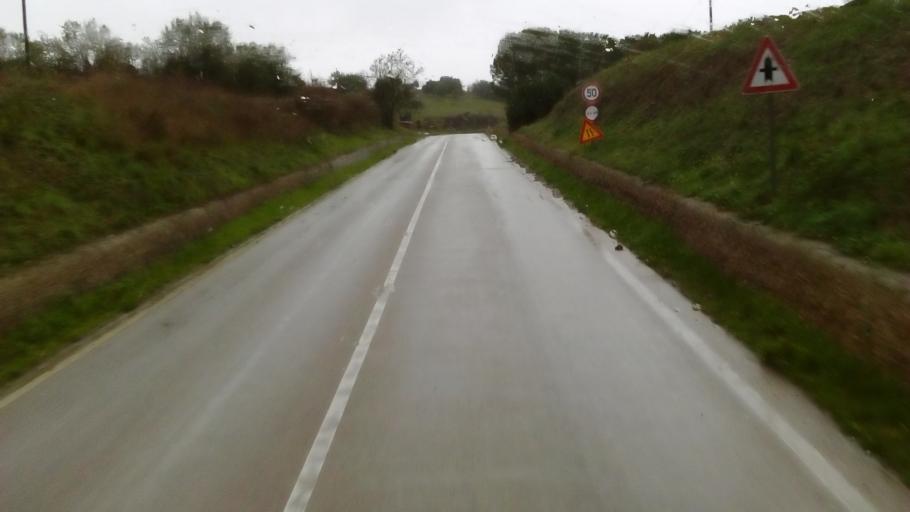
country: IT
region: Sicily
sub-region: Enna
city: Pietraperzia
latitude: 37.4307
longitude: 14.1694
